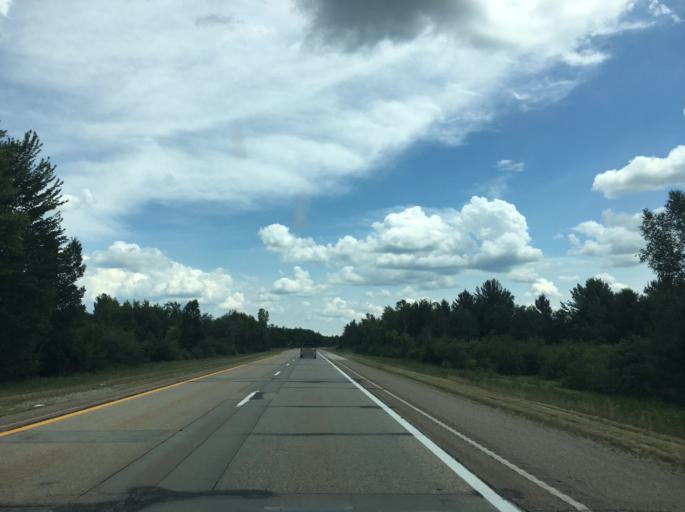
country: US
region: Michigan
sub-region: Ogemaw County
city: Skidway Lake
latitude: 44.1666
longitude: -84.1655
